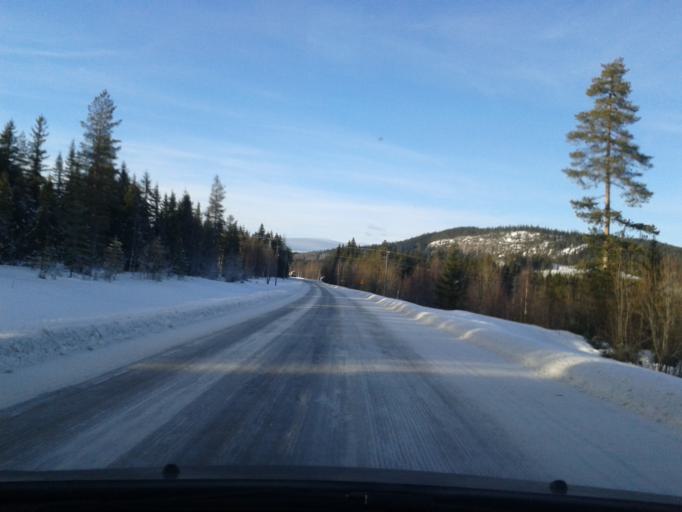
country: SE
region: Vaesterbotten
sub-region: Asele Kommun
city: Asele
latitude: 63.7800
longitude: 17.6651
